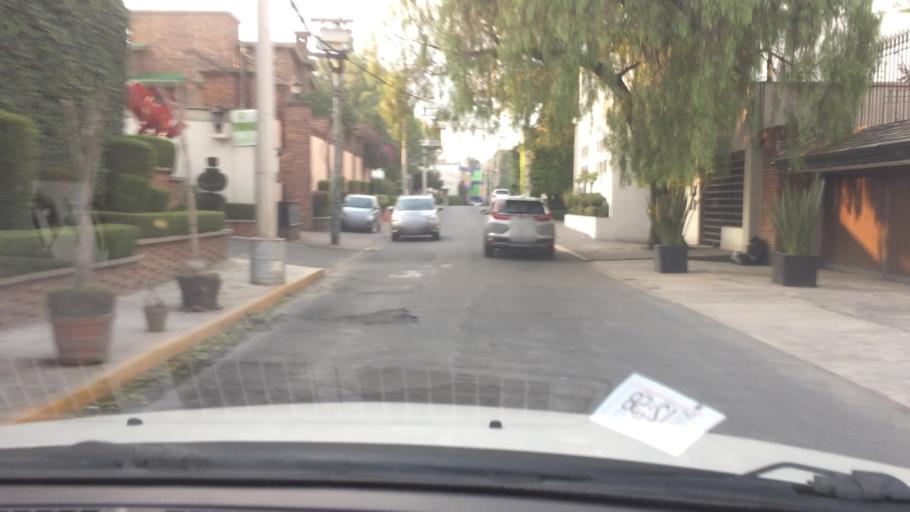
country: MX
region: Mexico City
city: Magdalena Contreras
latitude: 19.3227
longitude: -99.2119
